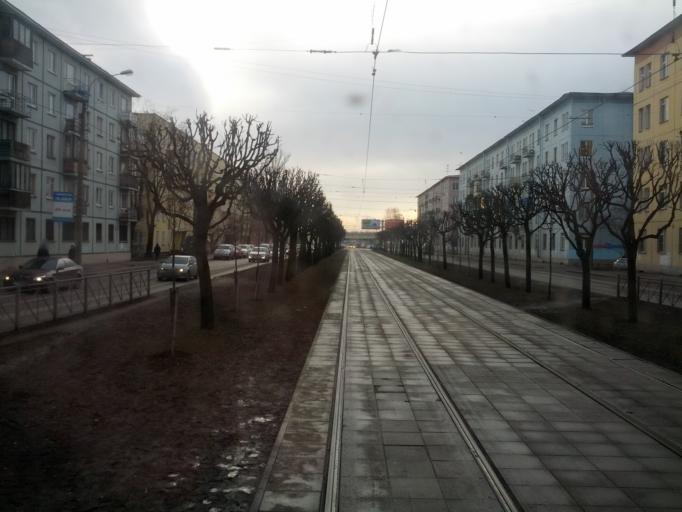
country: RU
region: St.-Petersburg
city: Centralniy
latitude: 59.9220
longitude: 30.4199
